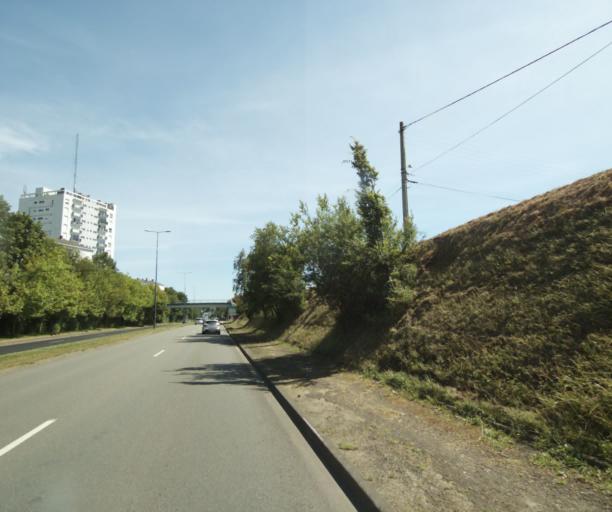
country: FR
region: Pays de la Loire
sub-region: Departement de la Mayenne
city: Laval
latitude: 48.0668
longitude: -0.7896
